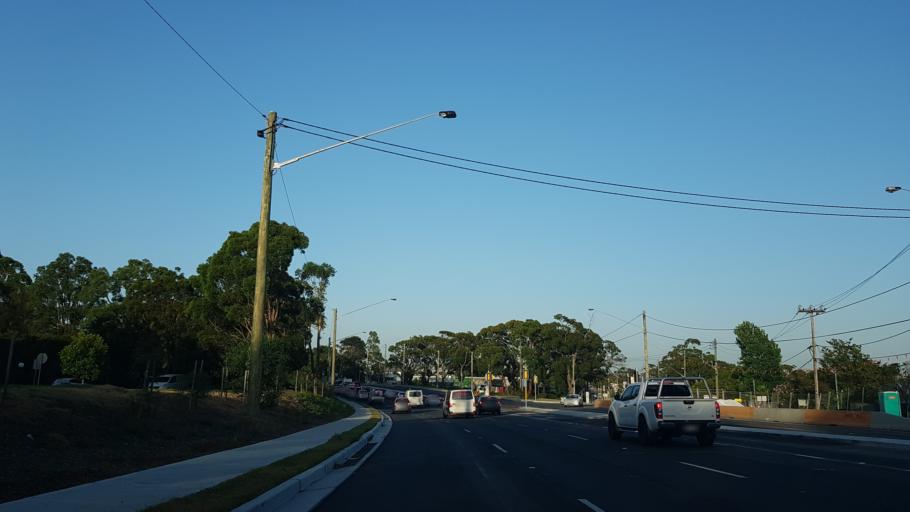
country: AU
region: New South Wales
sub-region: Warringah
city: Allambie Heights
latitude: -33.7519
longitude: 151.2468
